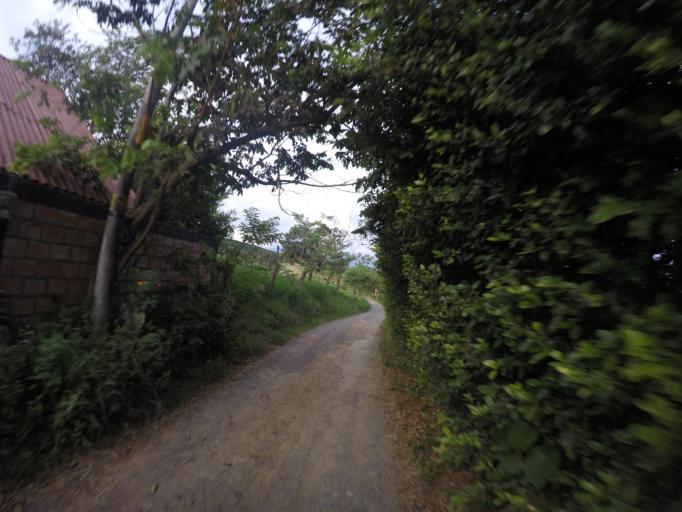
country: CO
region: Valle del Cauca
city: Ulloa
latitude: 4.7134
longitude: -75.7220
